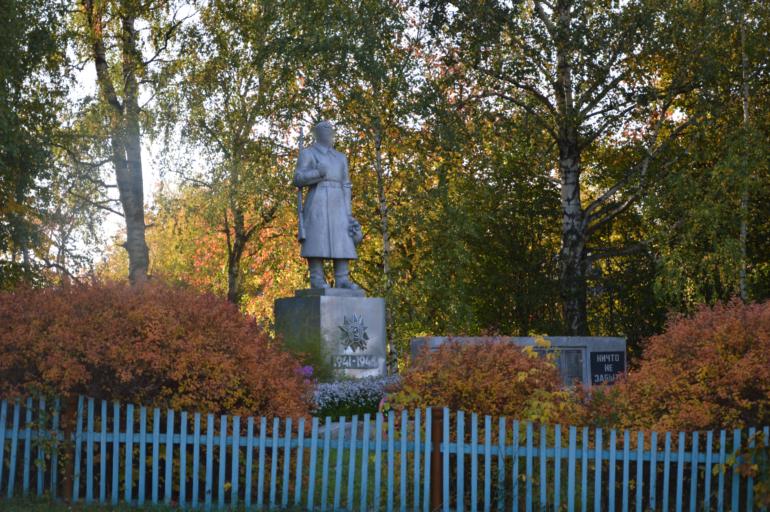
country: RU
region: Mariy-El
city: Sernur
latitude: 57.0475
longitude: 49.2580
